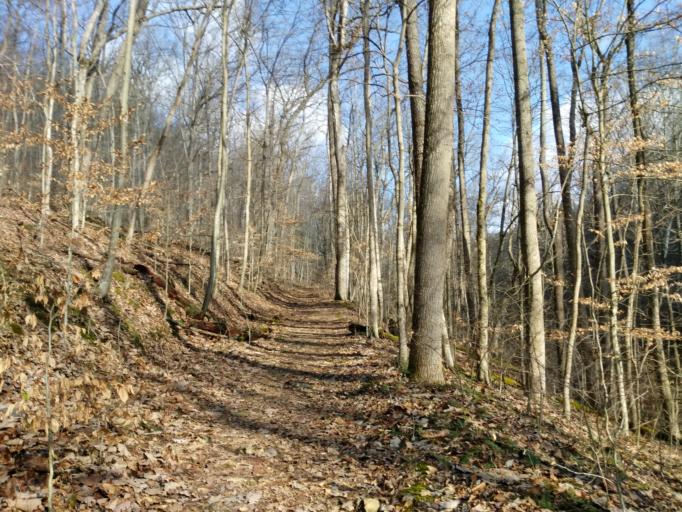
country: US
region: Ohio
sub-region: Fairfield County
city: Lancaster
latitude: 39.6481
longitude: -82.6433
